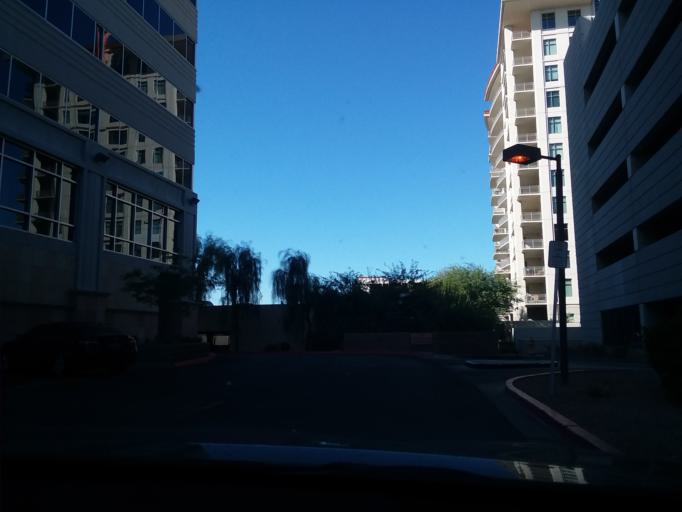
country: US
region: Arizona
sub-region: Maricopa County
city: Phoenix
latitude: 33.5074
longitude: -112.0319
